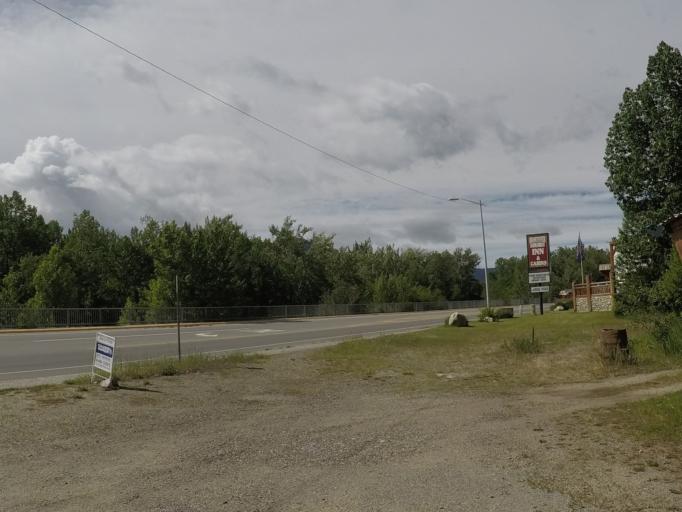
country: US
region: Montana
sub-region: Carbon County
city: Red Lodge
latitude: 45.1742
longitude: -109.2504
